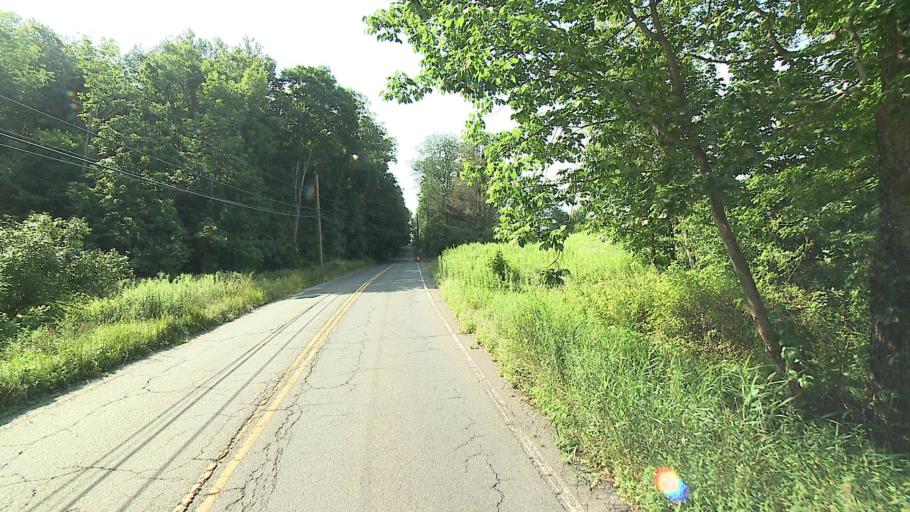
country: US
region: New York
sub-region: Putnam County
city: Putnam Lake
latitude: 41.4940
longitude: -73.5287
